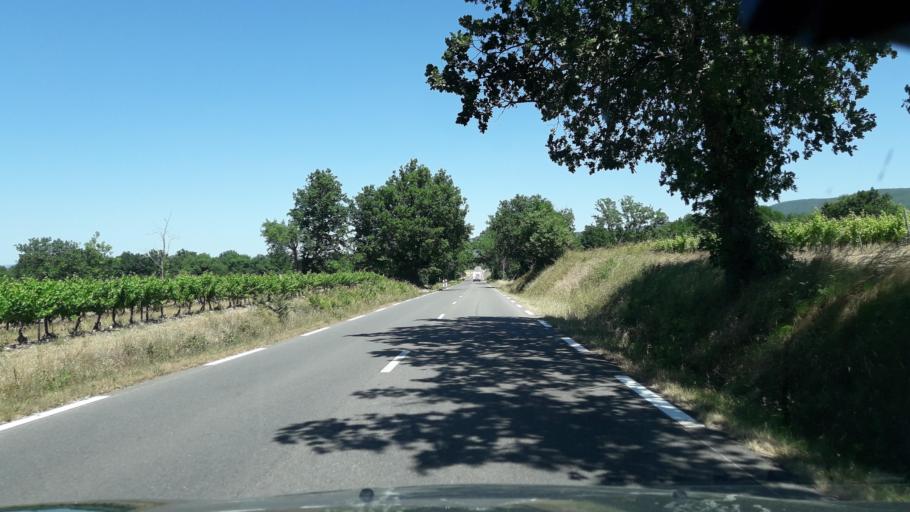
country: FR
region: Rhone-Alpes
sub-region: Departement de l'Ardeche
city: Lablachere
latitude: 44.3834
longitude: 4.2356
